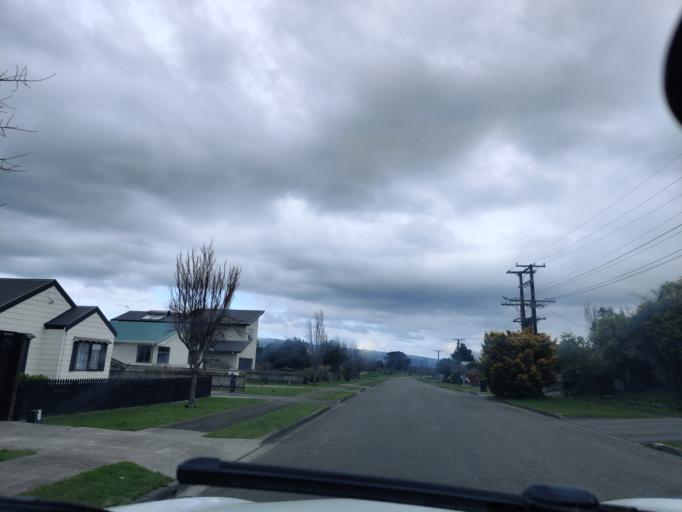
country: NZ
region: Manawatu-Wanganui
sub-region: Palmerston North City
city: Palmerston North
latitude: -40.2906
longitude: 175.7598
